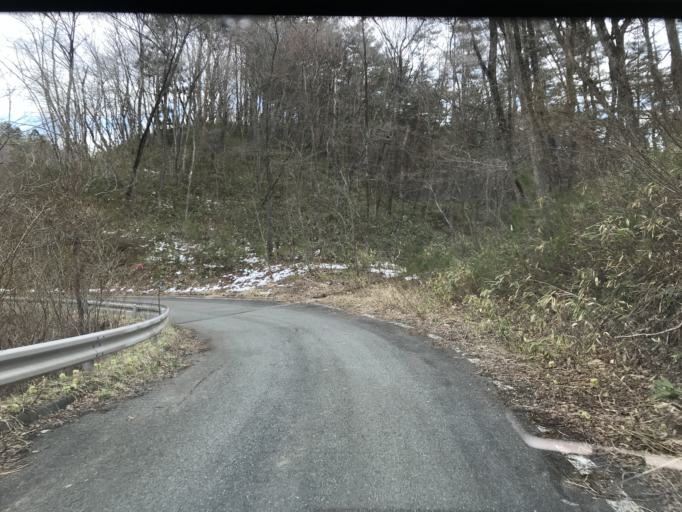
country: JP
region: Iwate
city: Ichinoseki
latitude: 38.9544
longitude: 141.0682
